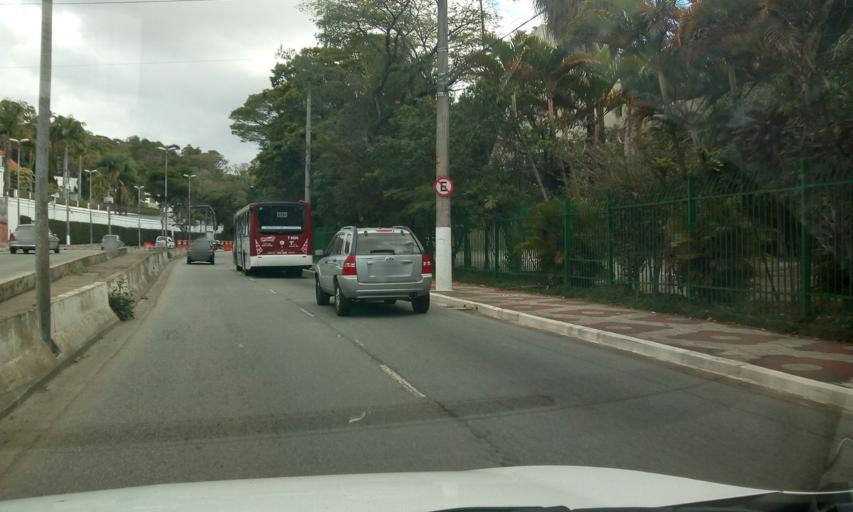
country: BR
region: Sao Paulo
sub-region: Sao Paulo
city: Sao Paulo
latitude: -23.5872
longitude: -46.6991
